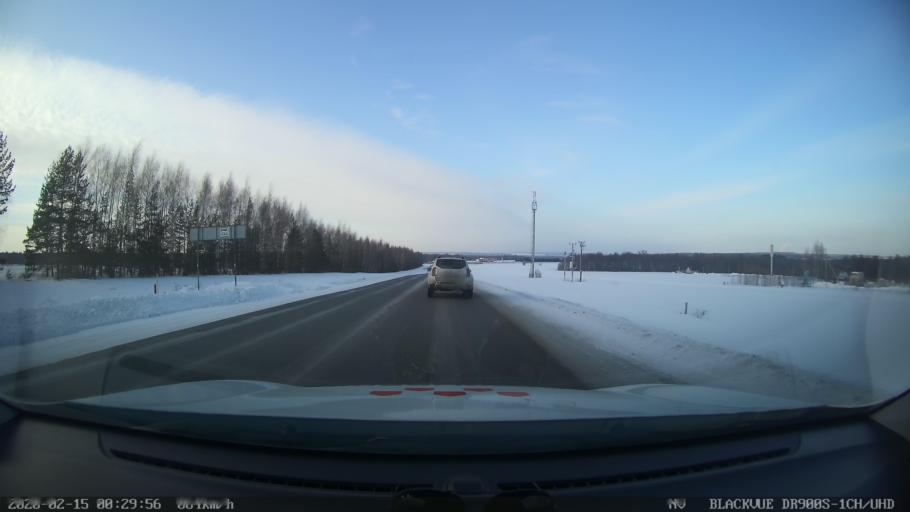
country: RU
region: Tatarstan
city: Verkhniy Uslon
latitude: 55.6550
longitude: 48.8629
